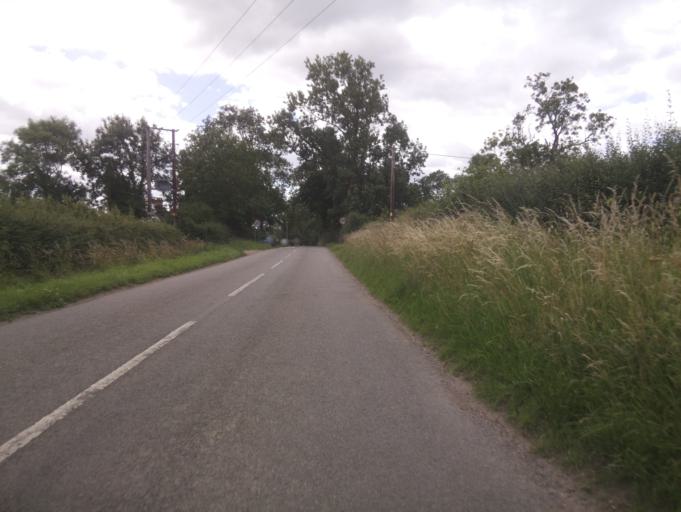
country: GB
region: England
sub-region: Nottinghamshire
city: Ruddington
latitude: 52.8441
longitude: -1.1030
